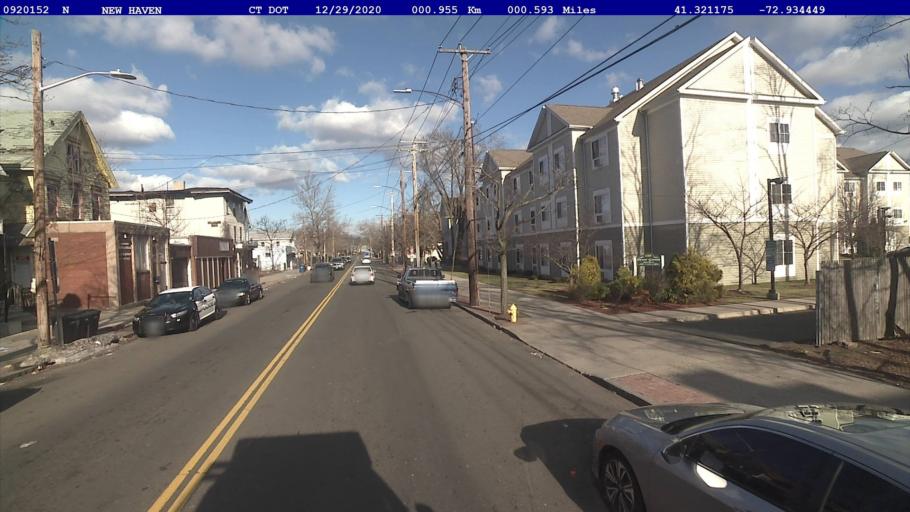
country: US
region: Connecticut
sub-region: New Haven County
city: New Haven
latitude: 41.3212
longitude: -72.9345
